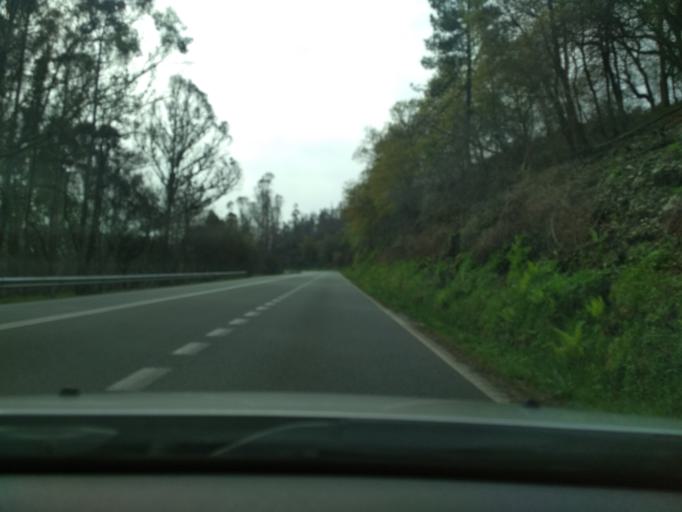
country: ES
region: Galicia
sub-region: Provincia de Pontevedra
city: Catoira
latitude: 42.6522
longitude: -8.6802
